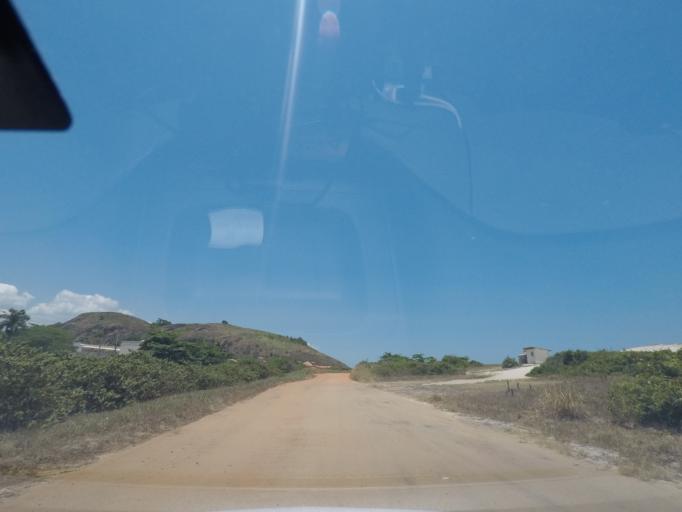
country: BR
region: Rio de Janeiro
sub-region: Niteroi
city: Niteroi
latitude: -22.9687
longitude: -43.0052
